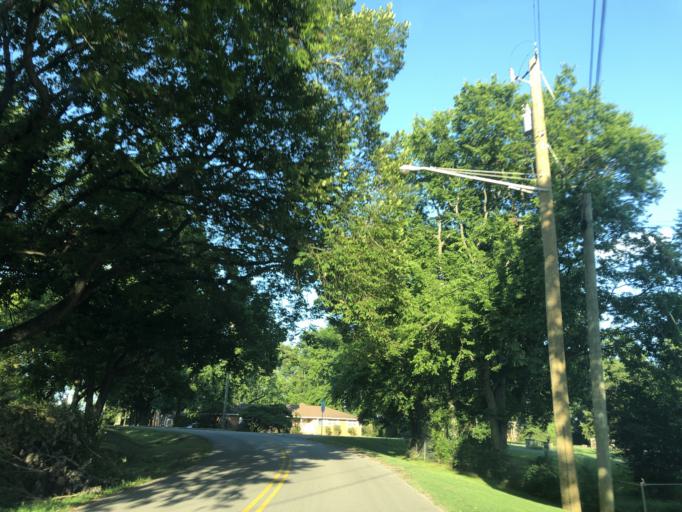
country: US
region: Tennessee
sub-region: Davidson County
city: Nashville
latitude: 36.1869
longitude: -86.8339
